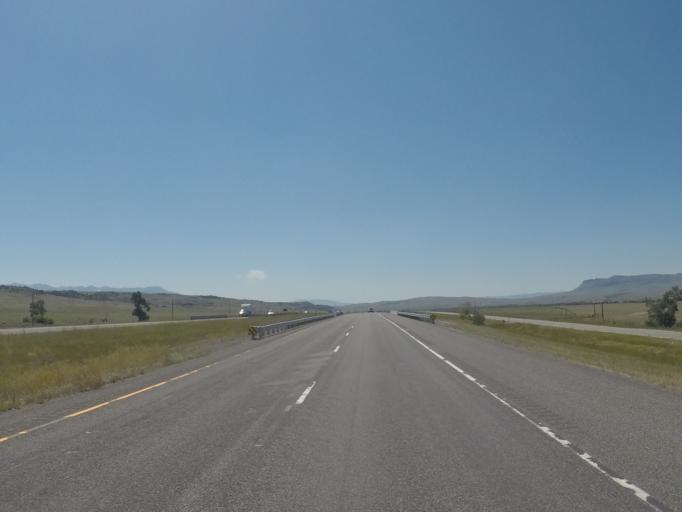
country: US
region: Montana
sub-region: Sweet Grass County
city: Big Timber
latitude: 45.7517
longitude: -110.1565
